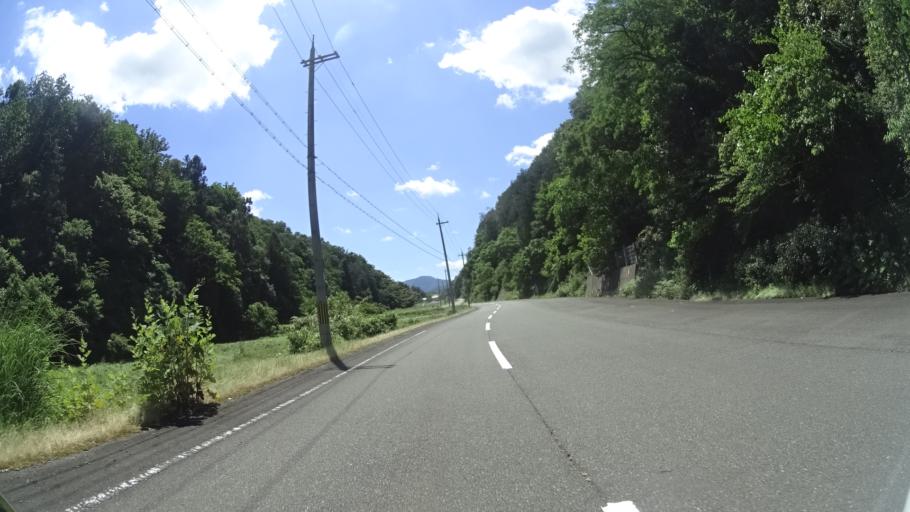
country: JP
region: Kyoto
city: Miyazu
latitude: 35.4202
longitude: 135.1783
